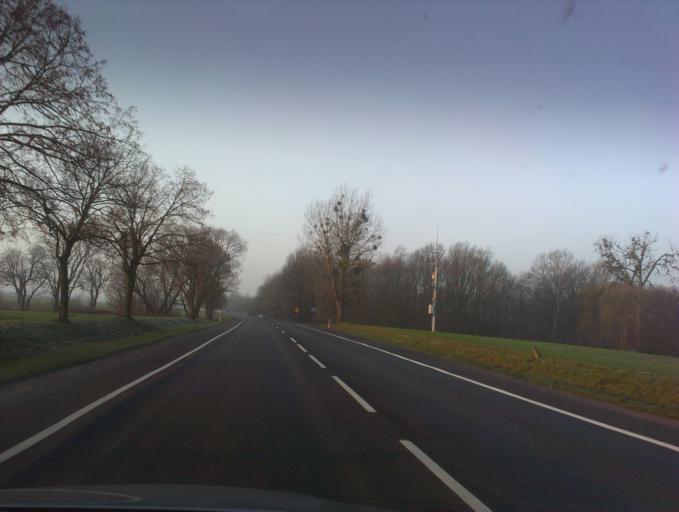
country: PL
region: Greater Poland Voivodeship
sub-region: Powiat obornicki
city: Oborniki
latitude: 52.6912
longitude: 16.8885
